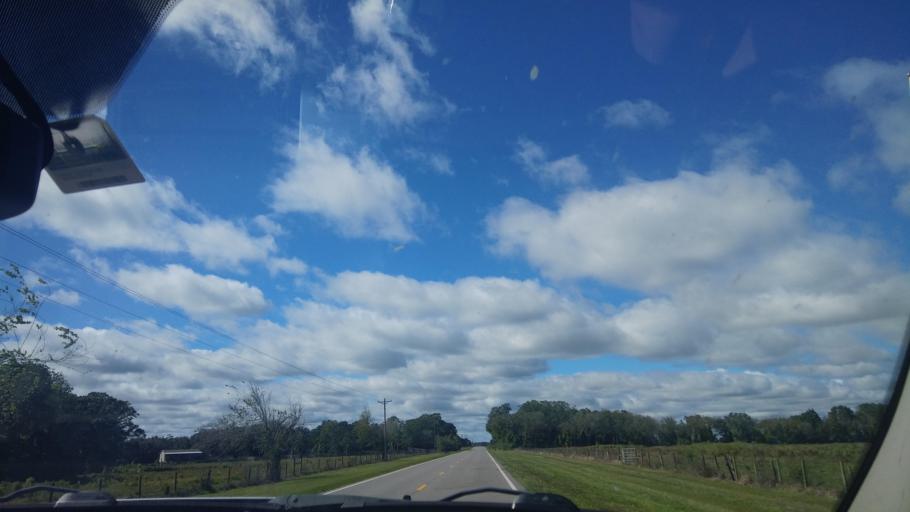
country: US
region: Florida
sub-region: Okeechobee County
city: Cypress Quarters
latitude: 27.3904
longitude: -80.8311
